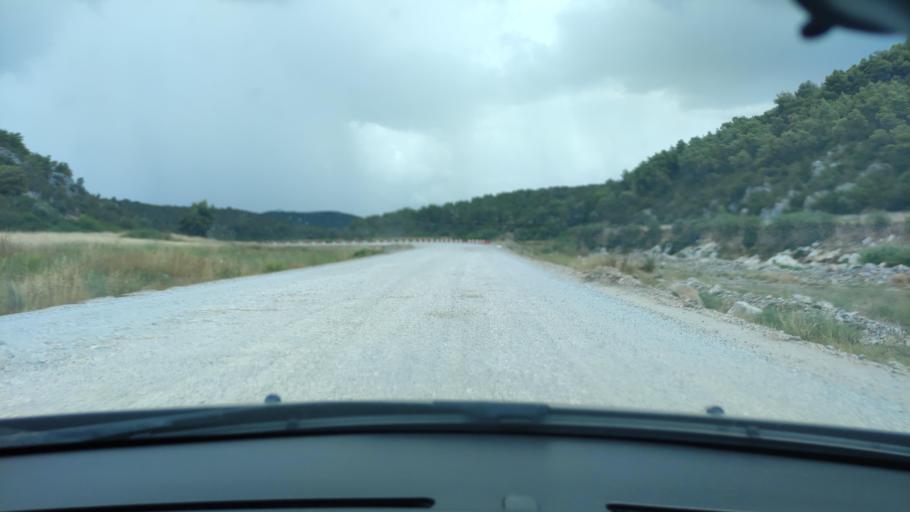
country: GR
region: Central Greece
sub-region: Nomos Evvoias
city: Afration
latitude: 38.5056
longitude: 23.7015
